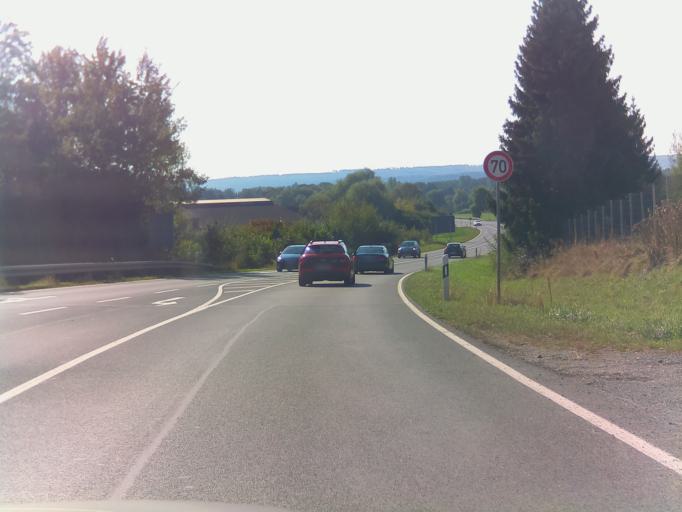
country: DE
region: Bavaria
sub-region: Upper Franconia
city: Hochstadt am Main
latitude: 50.1596
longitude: 11.1841
